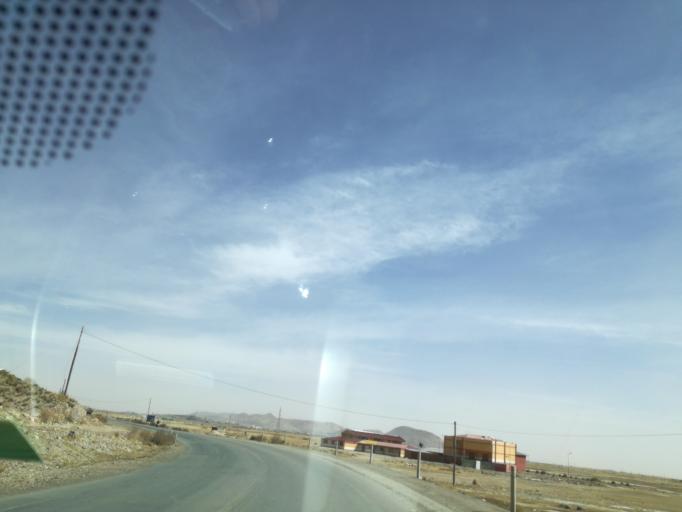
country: BO
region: Oruro
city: Oruro
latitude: -17.8942
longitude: -67.0465
